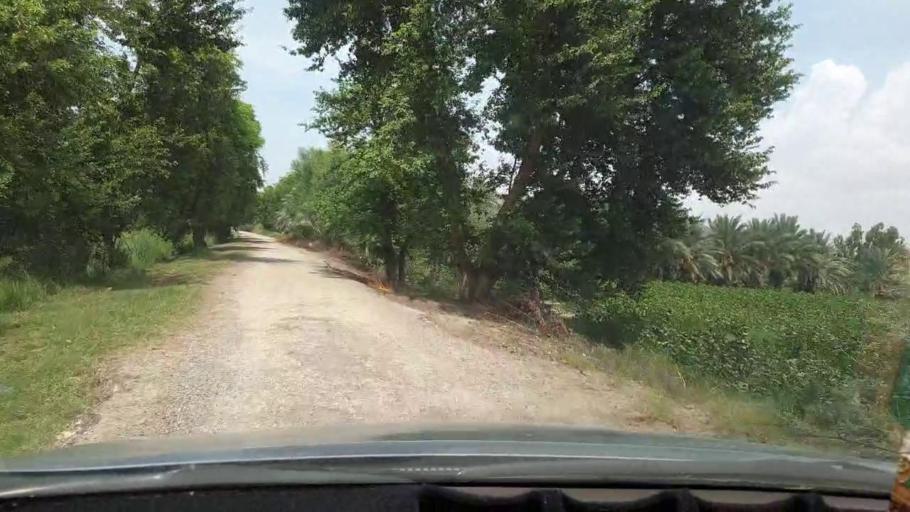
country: PK
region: Sindh
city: Khairpur
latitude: 27.4603
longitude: 68.8031
